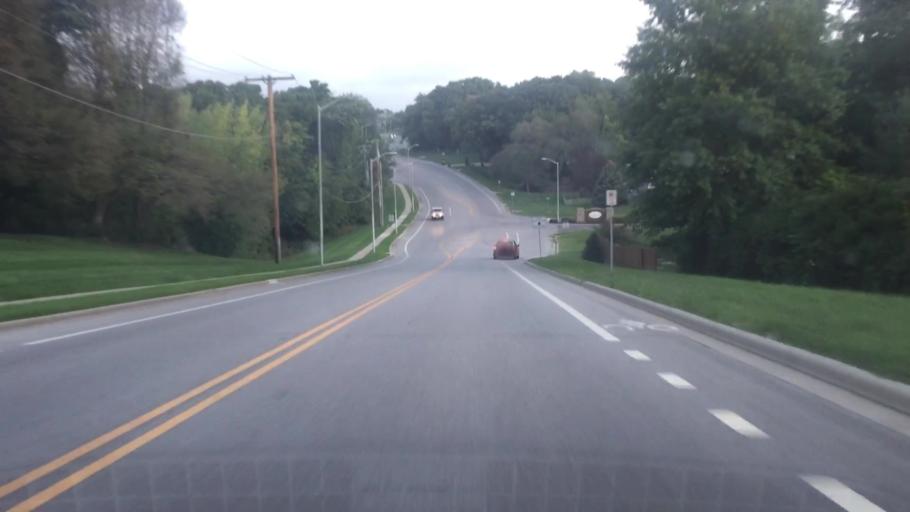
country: US
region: Kansas
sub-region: Johnson County
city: Shawnee
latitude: 39.0375
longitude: -94.7512
